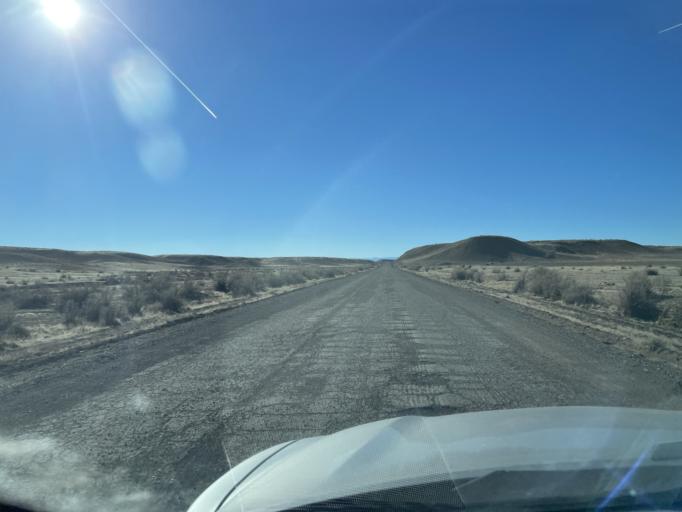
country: US
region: Colorado
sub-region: Mesa County
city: Loma
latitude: 39.2059
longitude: -109.0874
